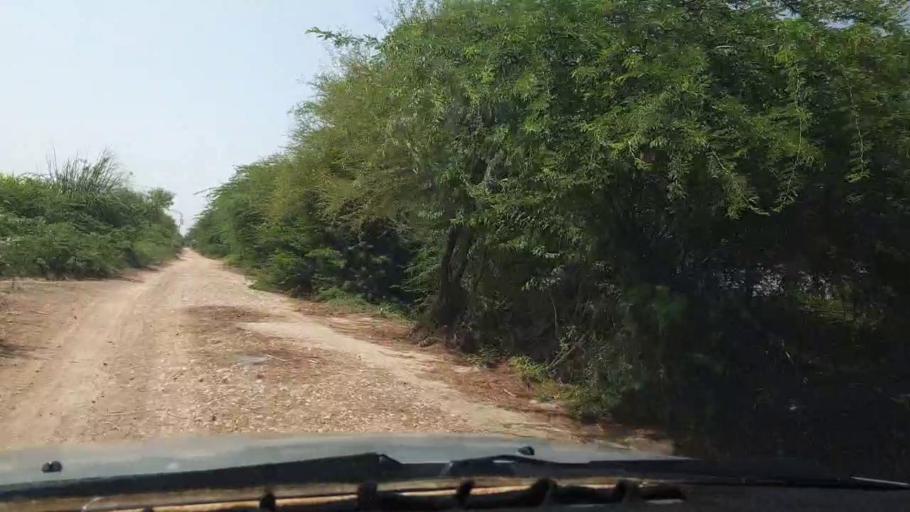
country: PK
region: Sindh
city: Tando Ghulam Ali
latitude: 25.1435
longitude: 68.7845
